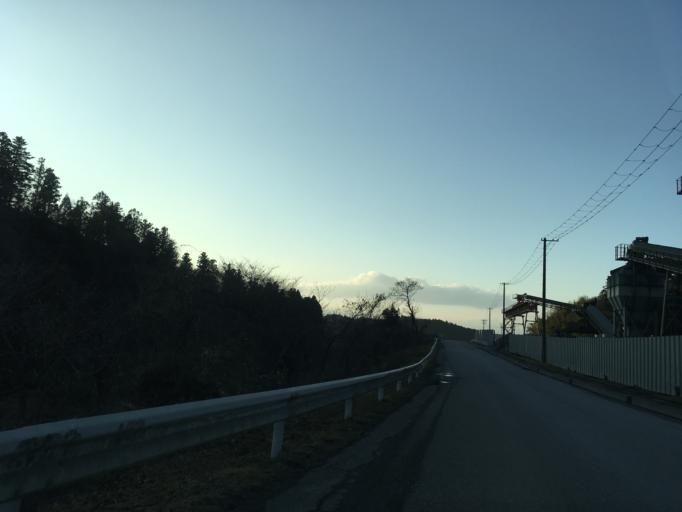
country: JP
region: Iwate
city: Ichinoseki
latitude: 38.8053
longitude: 141.2239
